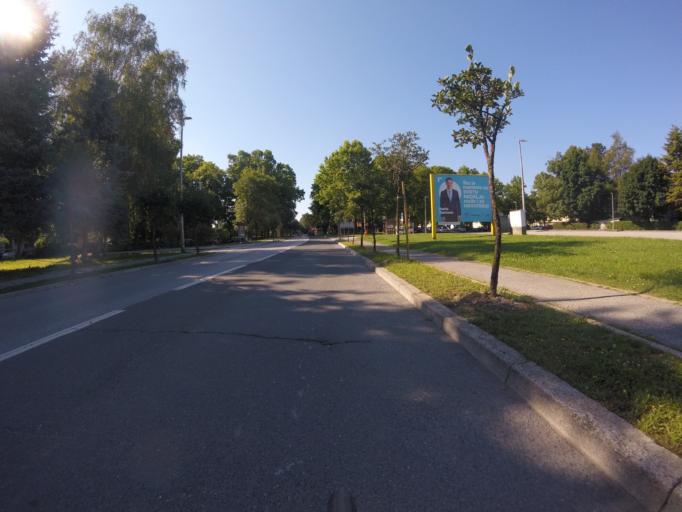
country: HR
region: Zagrebacka
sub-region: Grad Samobor
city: Samobor
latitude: 45.8040
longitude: 15.7137
